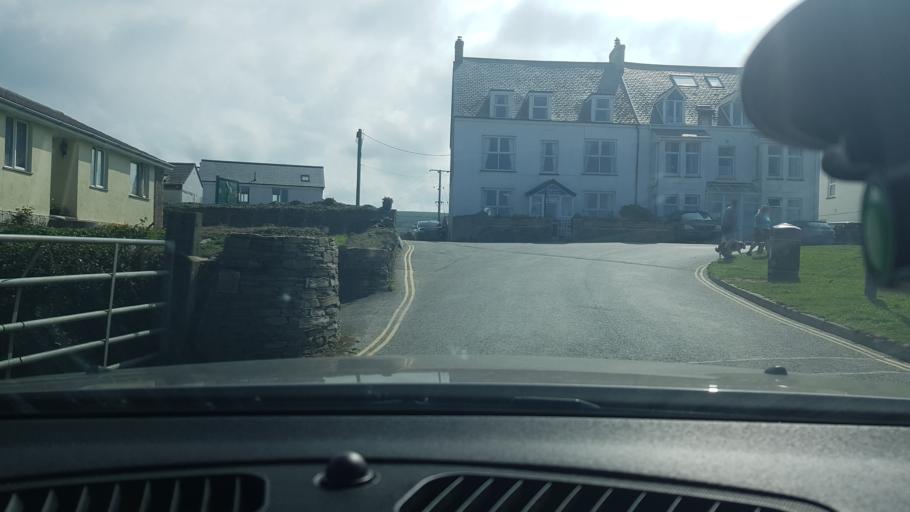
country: GB
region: England
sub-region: Cornwall
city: Tintagel
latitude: 50.6667
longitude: -4.7521
